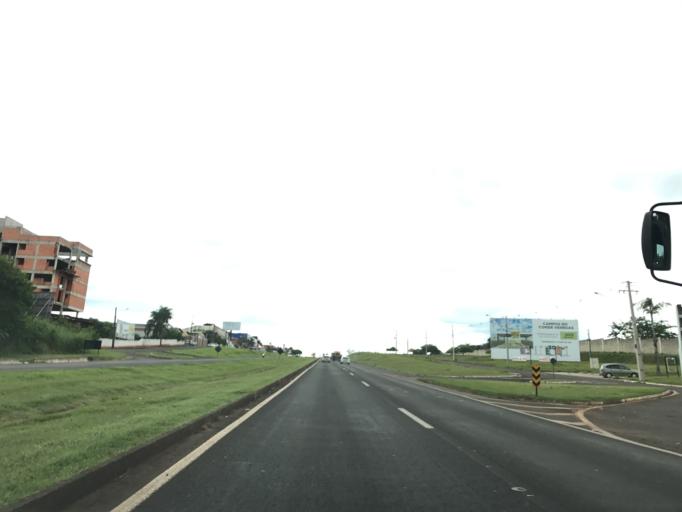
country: BR
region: Parana
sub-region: Cambe
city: Cambe
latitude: -23.2953
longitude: -51.2709
